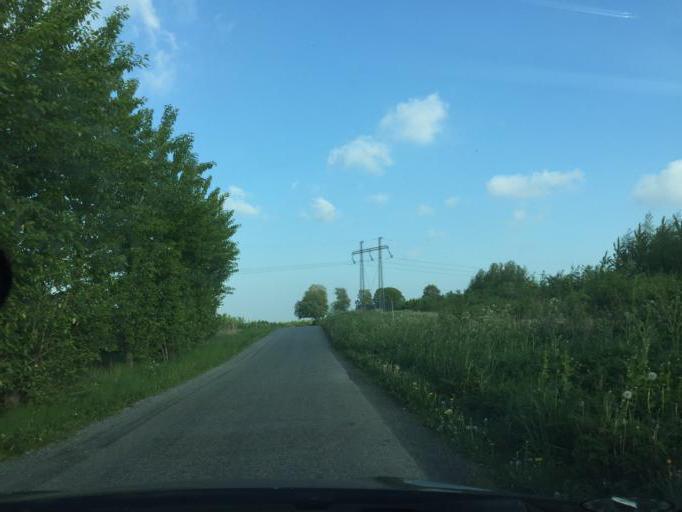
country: DK
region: South Denmark
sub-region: Odense Kommune
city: Bellinge
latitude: 55.3827
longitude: 10.2936
